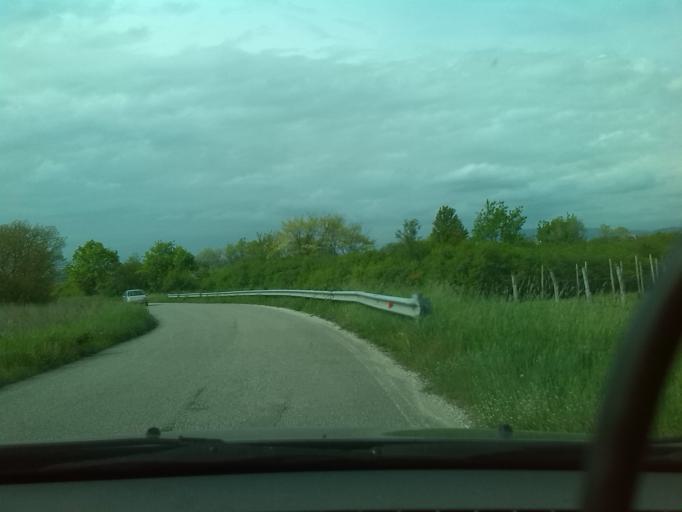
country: IT
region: Friuli Venezia Giulia
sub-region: Provincia di Gorizia
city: Capriva del Friuli
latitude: 45.9580
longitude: 13.5309
